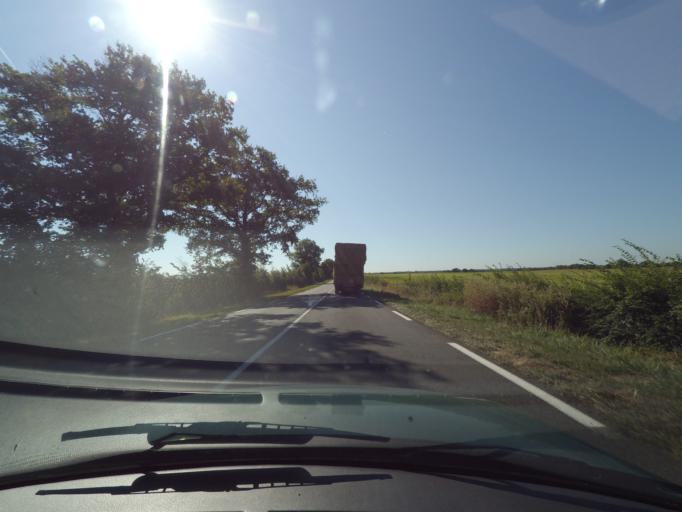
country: FR
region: Poitou-Charentes
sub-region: Departement de la Vienne
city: Lussac-les-Chateaux
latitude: 46.3795
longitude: 0.7527
